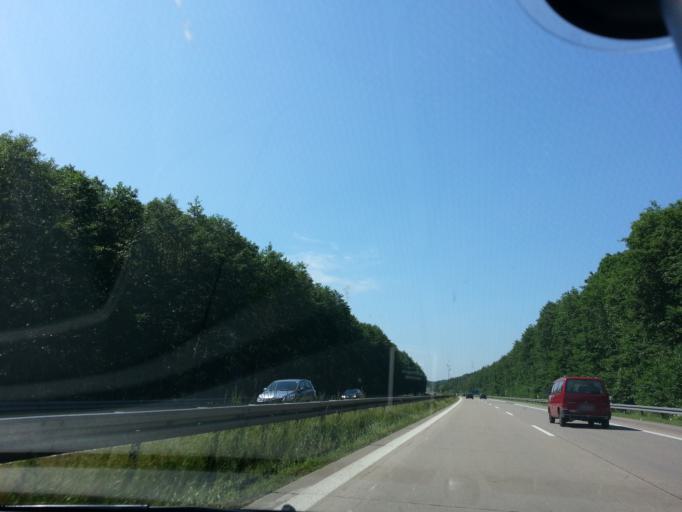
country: DE
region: Brandenburg
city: Putlitz
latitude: 53.2872
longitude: 12.0679
